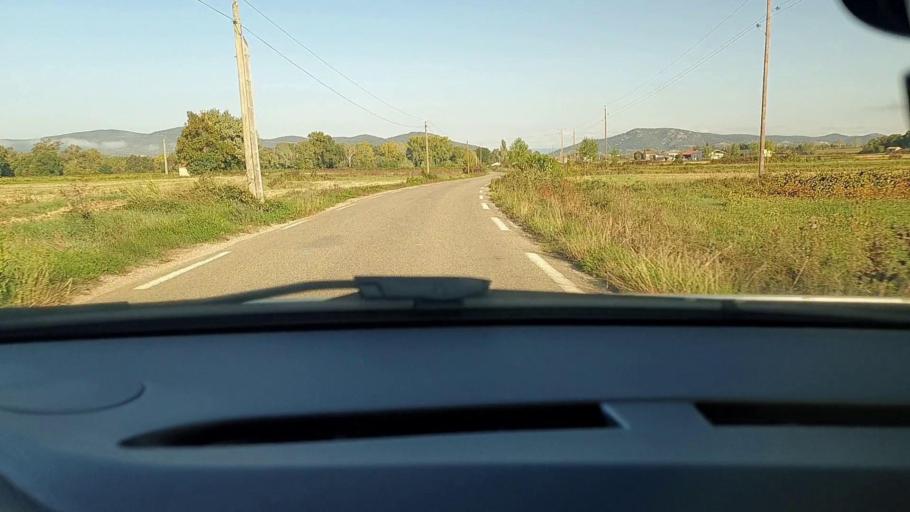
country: FR
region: Languedoc-Roussillon
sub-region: Departement du Gard
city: Saint-Ambroix
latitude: 44.2639
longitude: 4.2801
